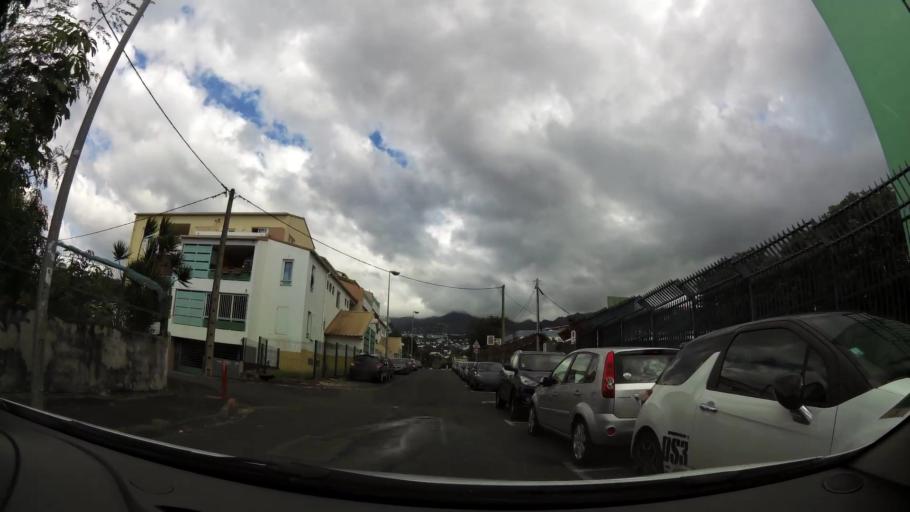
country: RE
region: Reunion
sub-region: Reunion
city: Saint-Denis
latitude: -20.8925
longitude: 55.4772
